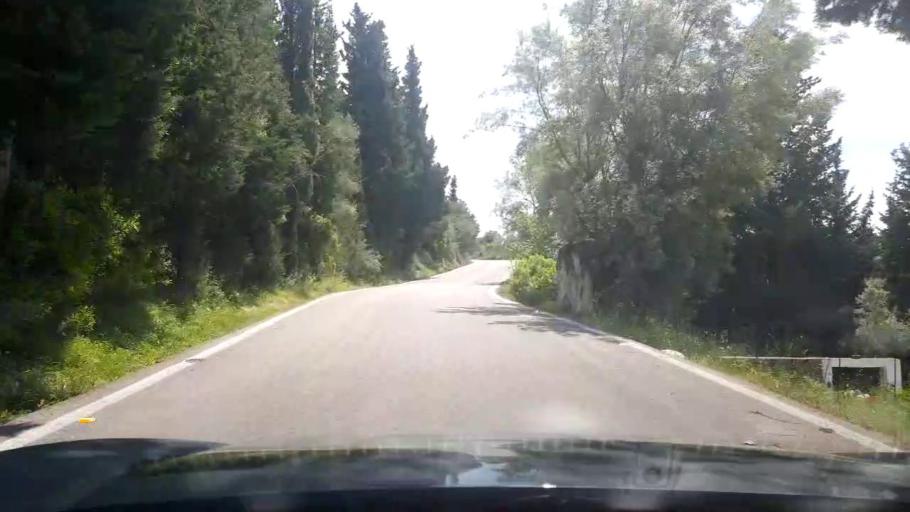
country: GR
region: Ionian Islands
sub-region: Lefkada
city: Nidri
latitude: 38.6501
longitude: 20.7082
